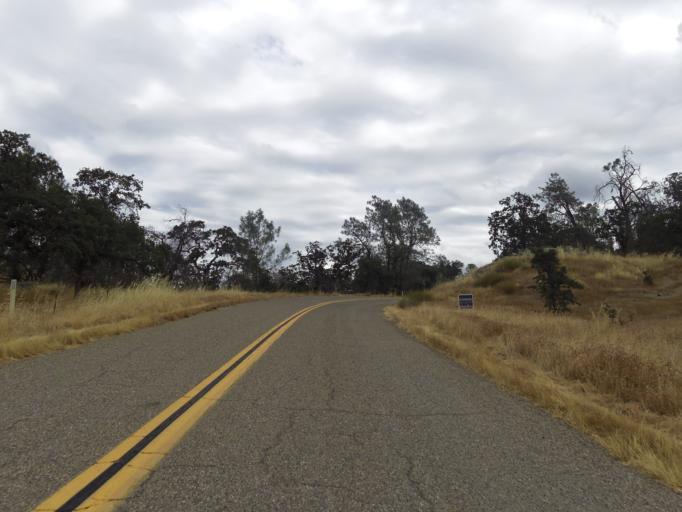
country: US
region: California
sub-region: Madera County
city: Yosemite Lakes
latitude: 37.2716
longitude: -119.8470
